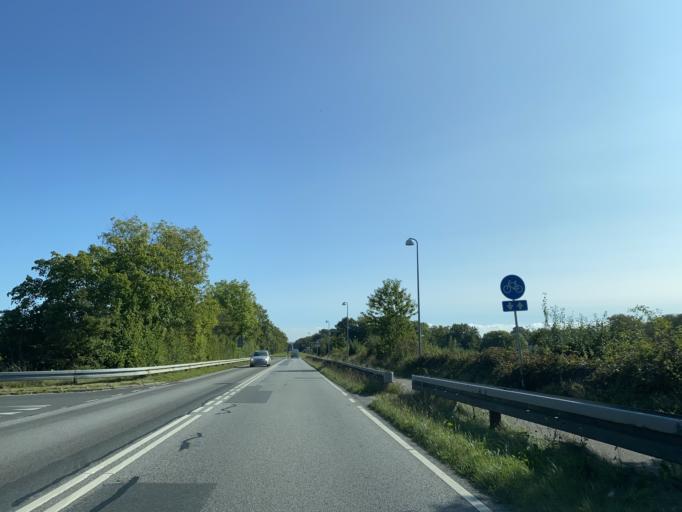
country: DK
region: South Denmark
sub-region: Aabenraa Kommune
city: Aabenraa
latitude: 55.0624
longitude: 9.3843
